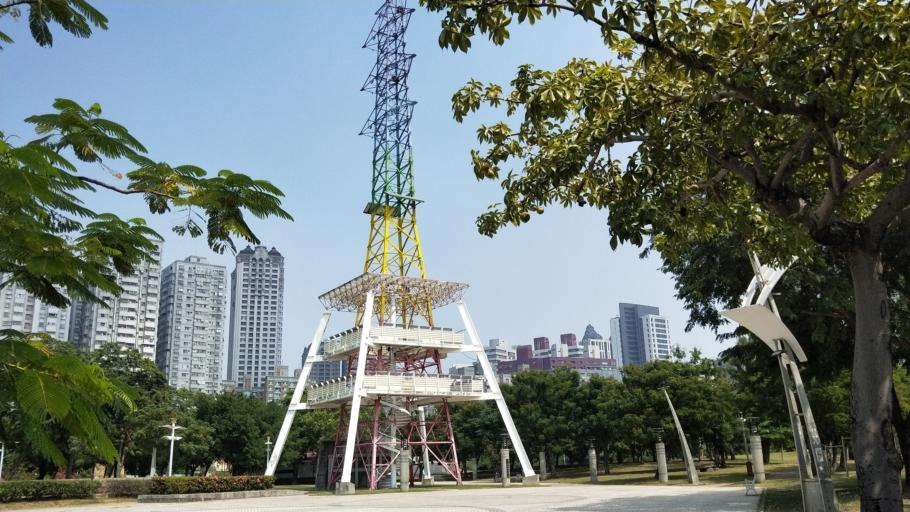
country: TW
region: Kaohsiung
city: Kaohsiung
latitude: 22.6510
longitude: 120.2962
